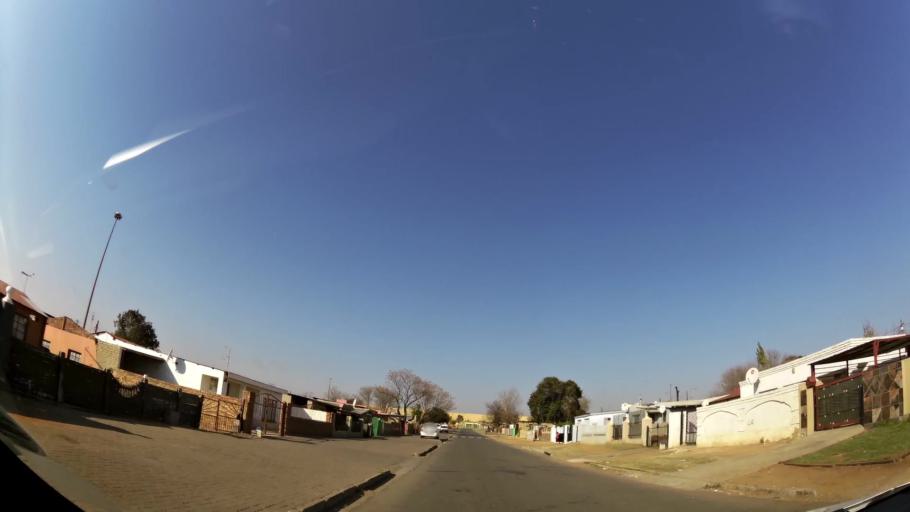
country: ZA
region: Gauteng
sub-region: Ekurhuleni Metropolitan Municipality
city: Boksburg
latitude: -26.2316
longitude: 28.2311
